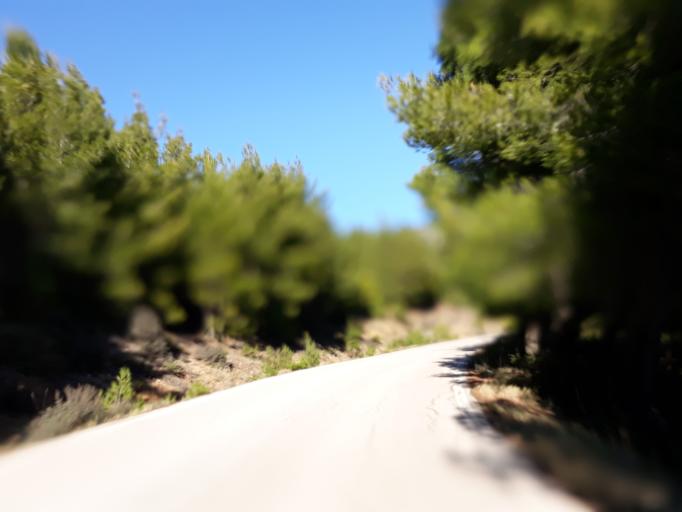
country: GR
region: Attica
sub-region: Nomarchia Dytikis Attikis
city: Fyli
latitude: 38.1245
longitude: 23.6481
